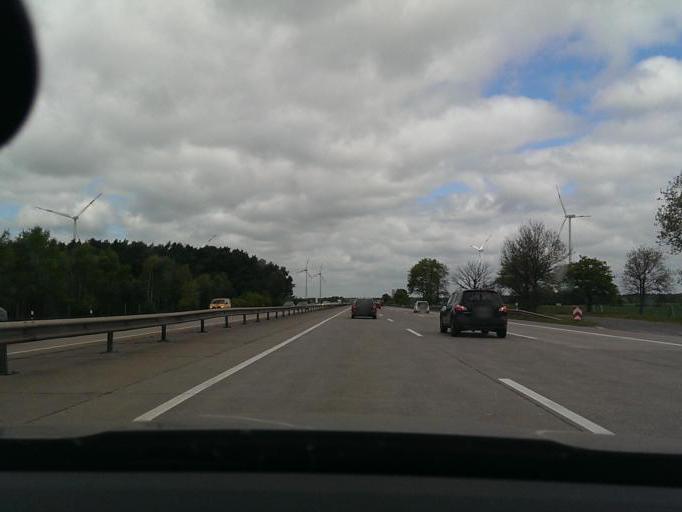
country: DE
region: Lower Saxony
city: Lindwedel
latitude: 52.6401
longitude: 9.7141
